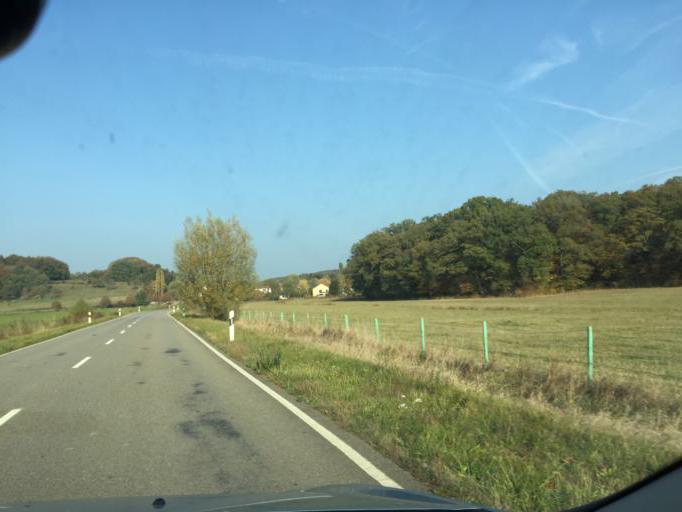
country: LU
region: Luxembourg
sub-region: Canton de Luxembourg
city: Contern
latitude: 49.5576
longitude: 6.2254
